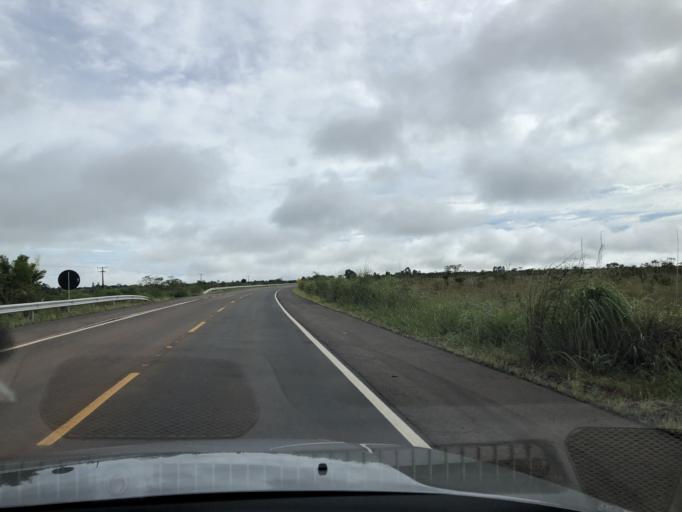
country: BR
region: Federal District
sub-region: Brasilia
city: Brasilia
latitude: -15.6299
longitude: -48.0757
